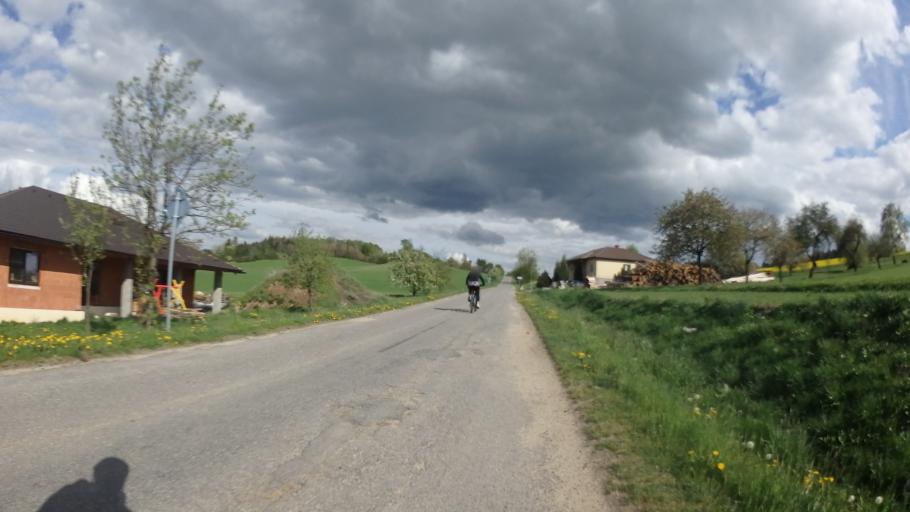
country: CZ
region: Vysocina
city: Merin
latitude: 49.3459
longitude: 15.8809
